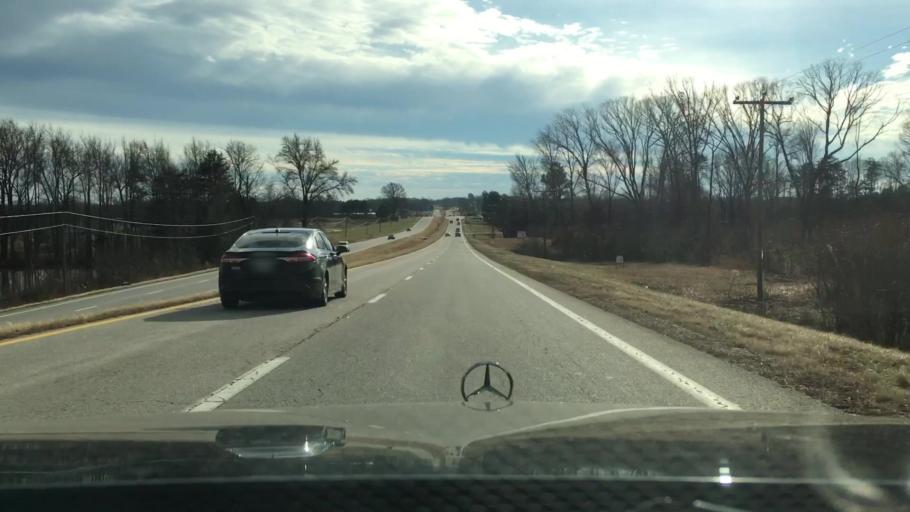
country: US
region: Virginia
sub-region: Pittsylvania County
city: Mount Hermon
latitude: 36.7409
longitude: -79.3791
